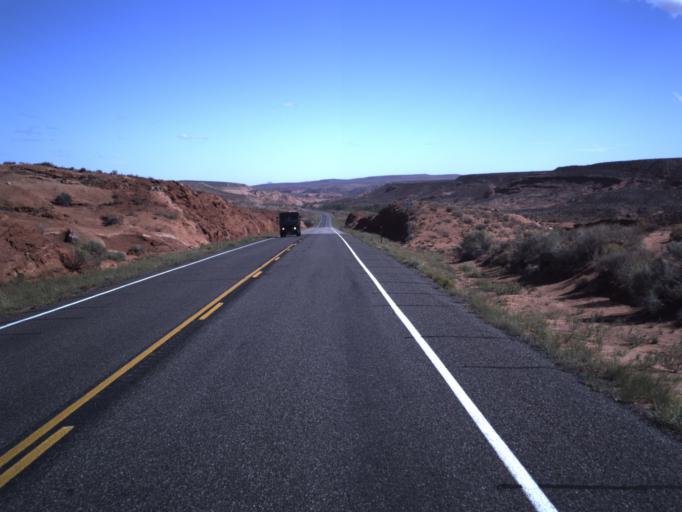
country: US
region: Utah
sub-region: Wayne County
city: Loa
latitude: 38.0655
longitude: -110.6020
